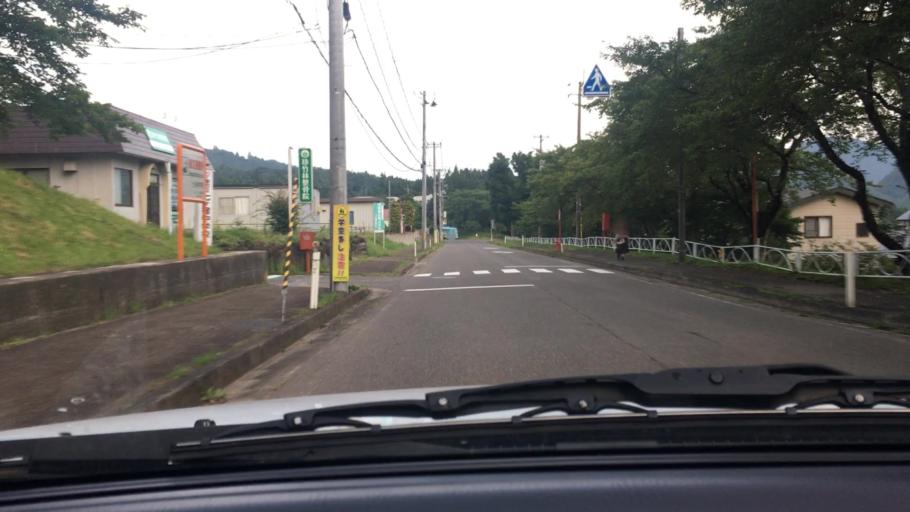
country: JP
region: Miyagi
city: Shiroishi
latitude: 37.9946
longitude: 140.4468
